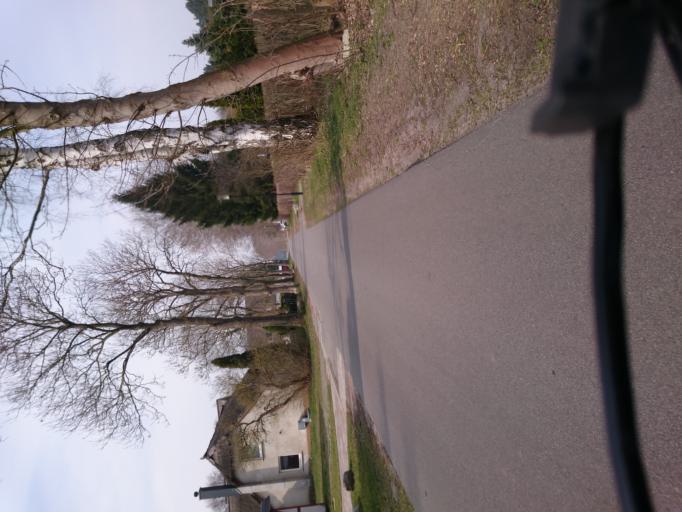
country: DE
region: Mecklenburg-Vorpommern
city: Barth
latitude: 54.3689
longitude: 12.6567
